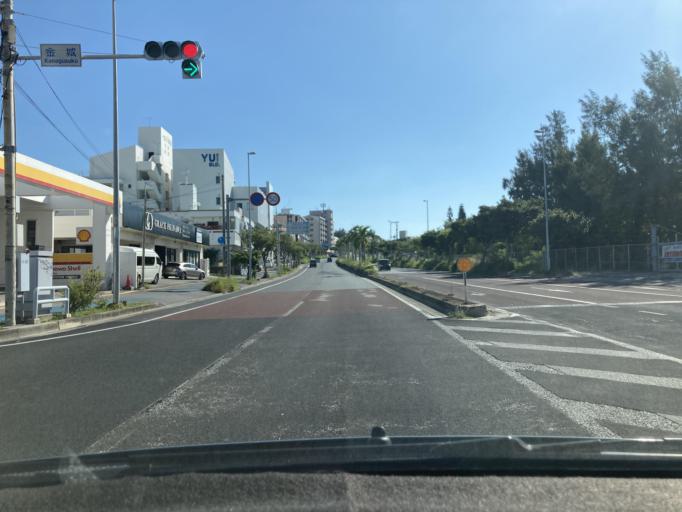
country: JP
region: Okinawa
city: Naha-shi
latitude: 26.2022
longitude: 127.6620
